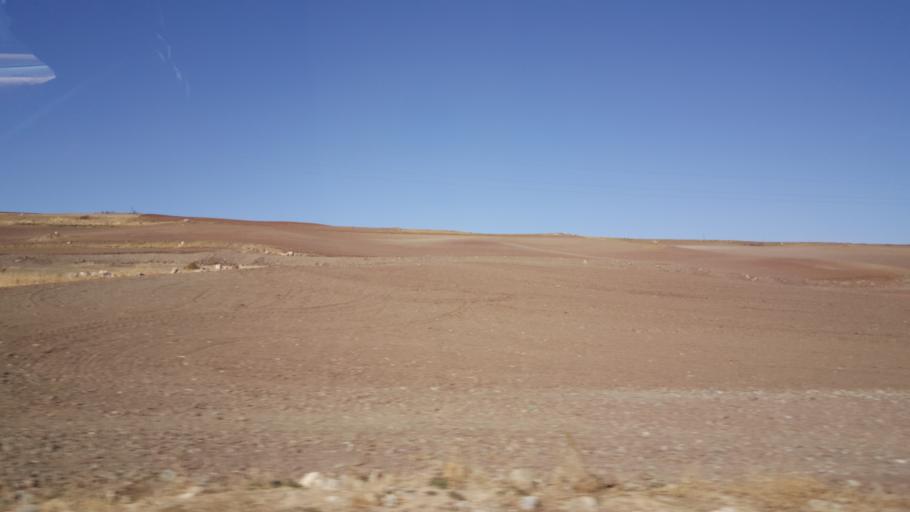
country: TR
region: Ankara
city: Ikizce
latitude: 39.5412
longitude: 32.6325
